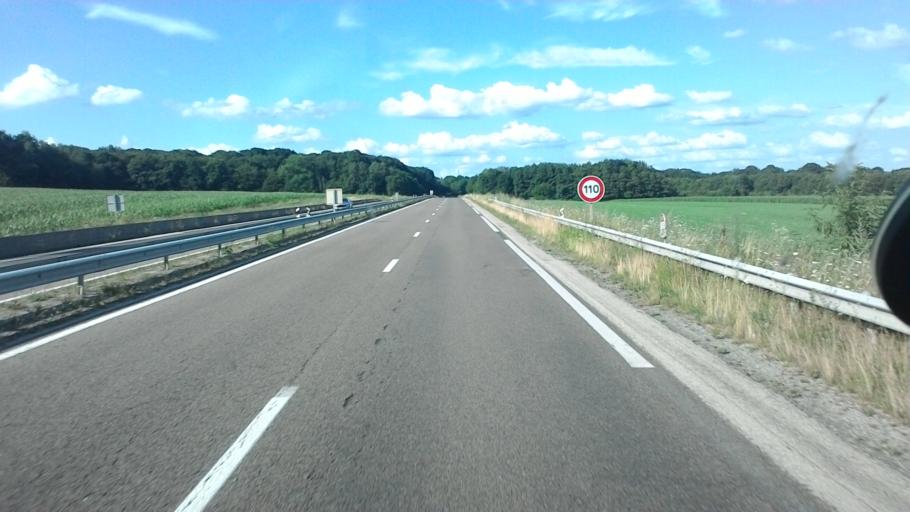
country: FR
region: Franche-Comte
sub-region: Departement de la Haute-Saone
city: Luxeuil-les-Bains
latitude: 47.7389
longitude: 6.3200
